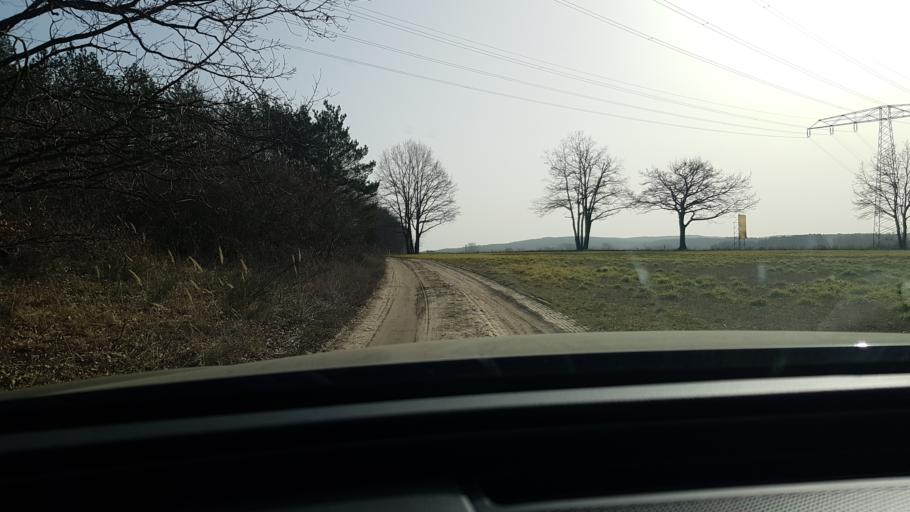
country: DE
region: Brandenburg
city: Schenkendobern
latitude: 51.9547
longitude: 14.6404
